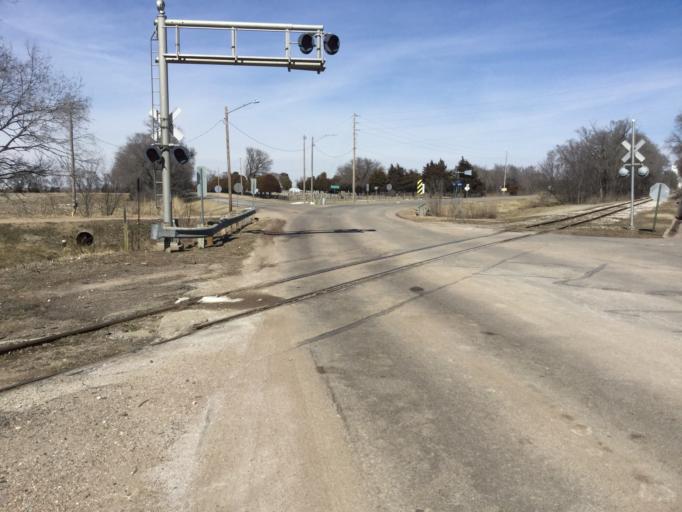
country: US
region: Kansas
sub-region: Sedgwick County
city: Clearwater
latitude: 37.5079
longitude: -97.5061
